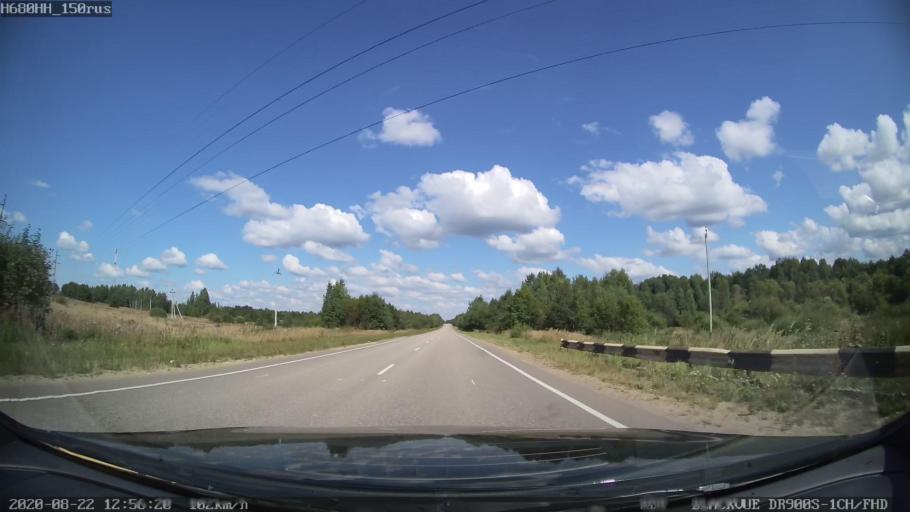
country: RU
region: Tverskaya
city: Rameshki
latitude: 57.5547
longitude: 36.3153
